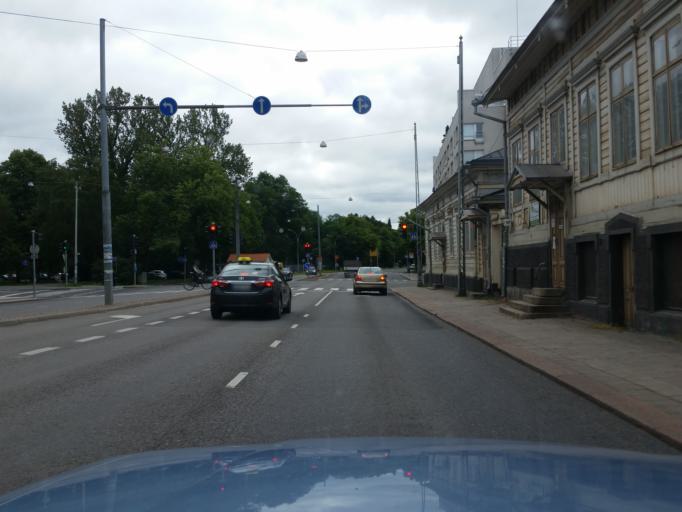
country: FI
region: Varsinais-Suomi
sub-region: Turku
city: Turku
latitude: 60.4469
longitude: 22.2829
